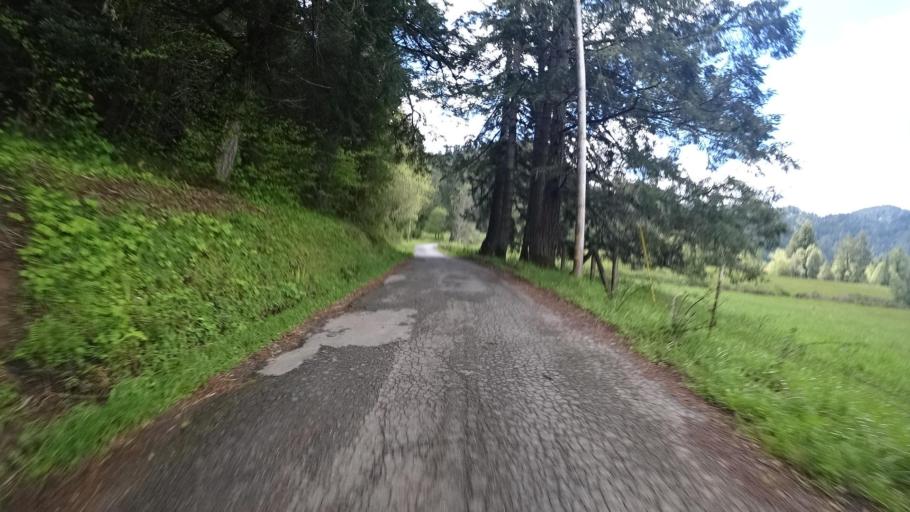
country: US
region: California
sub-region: Humboldt County
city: Blue Lake
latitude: 40.7655
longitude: -123.8955
